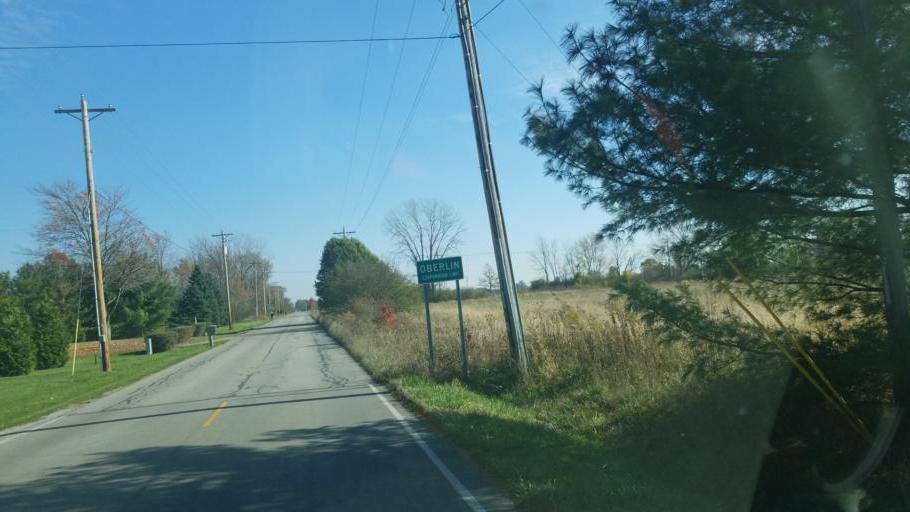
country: US
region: Ohio
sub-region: Lorain County
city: Oberlin
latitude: 41.2797
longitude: -82.2338
